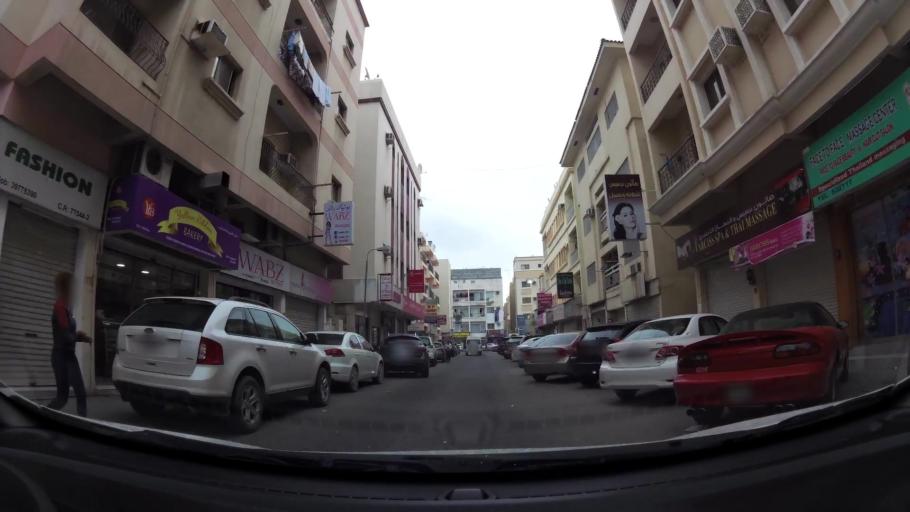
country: BH
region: Manama
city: Manama
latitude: 26.2353
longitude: 50.5916
